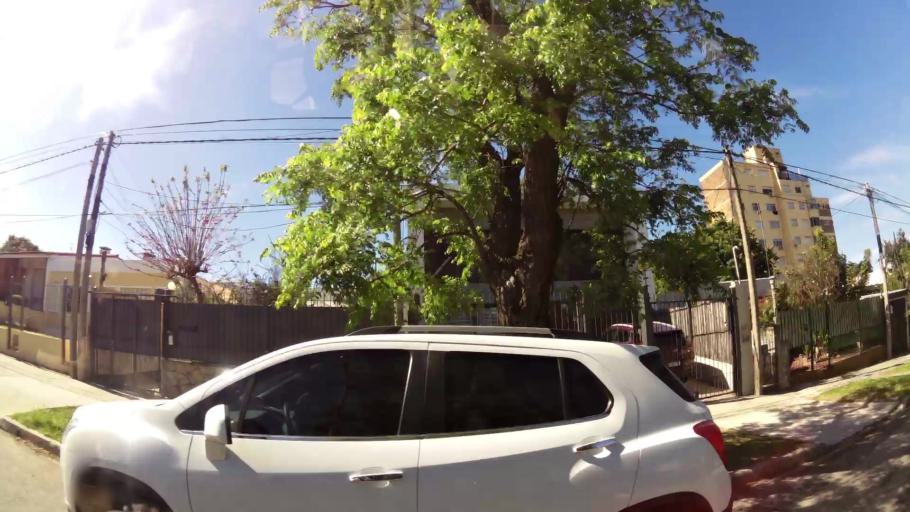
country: UY
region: Montevideo
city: Montevideo
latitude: -34.8917
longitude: -56.1210
